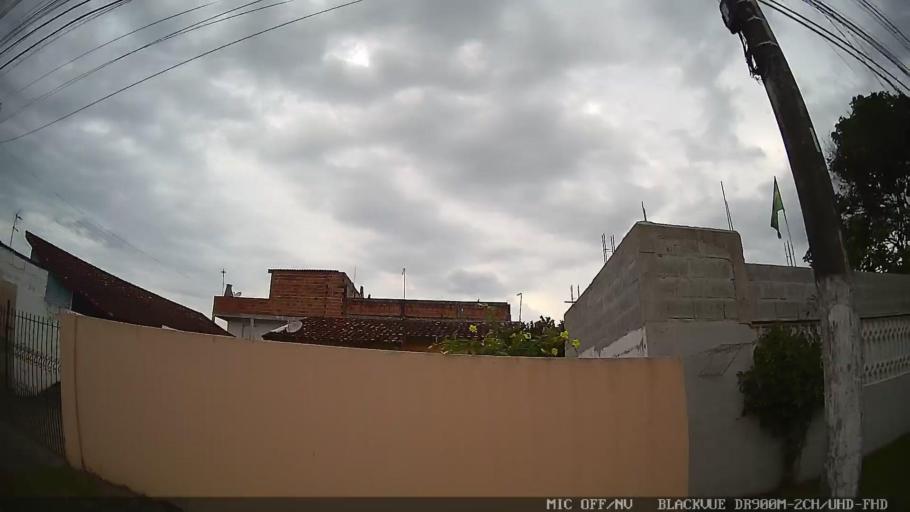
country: BR
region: Sao Paulo
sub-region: Caraguatatuba
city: Caraguatatuba
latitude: -23.6801
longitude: -45.4515
